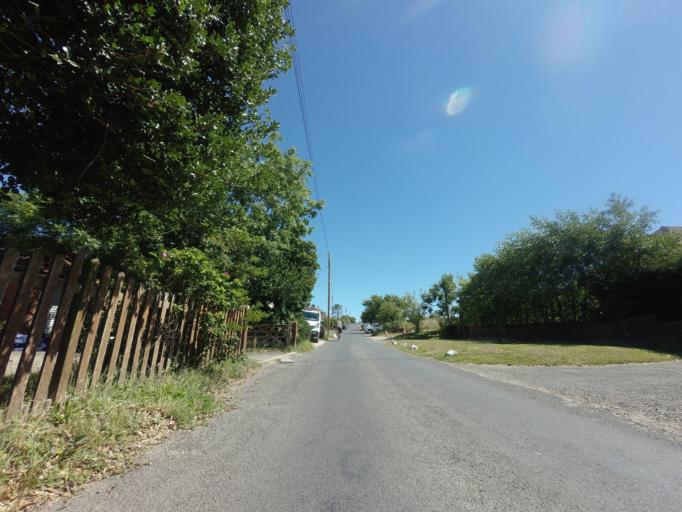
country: GB
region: England
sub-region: Kent
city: Eastry
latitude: 51.1993
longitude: 1.3223
